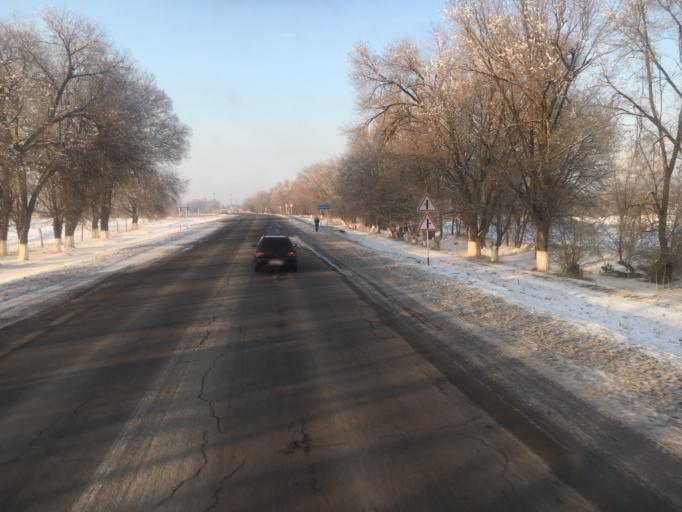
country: KZ
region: Almaty Oblysy
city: Burunday
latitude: 43.3291
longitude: 76.6622
